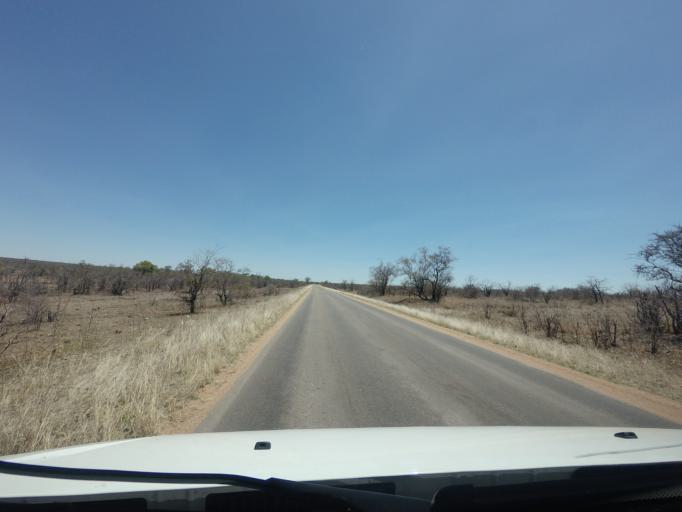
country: ZA
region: Limpopo
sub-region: Mopani District Municipality
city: Phalaborwa
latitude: -23.5920
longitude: 31.4533
